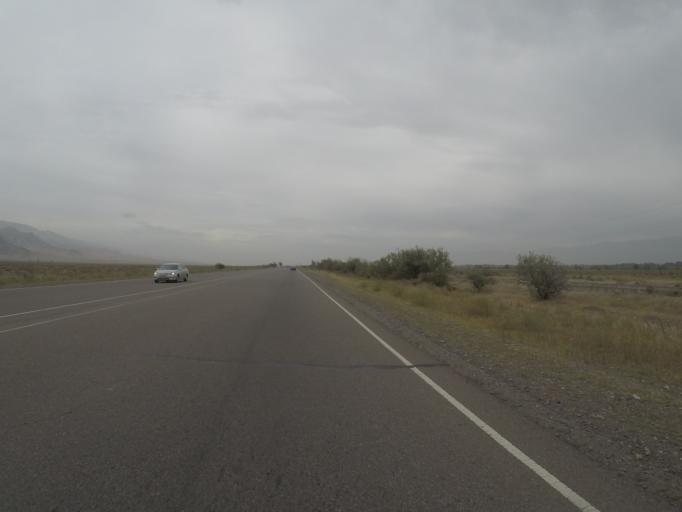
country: KG
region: Chuy
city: Tokmok
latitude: 42.8298
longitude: 75.4676
